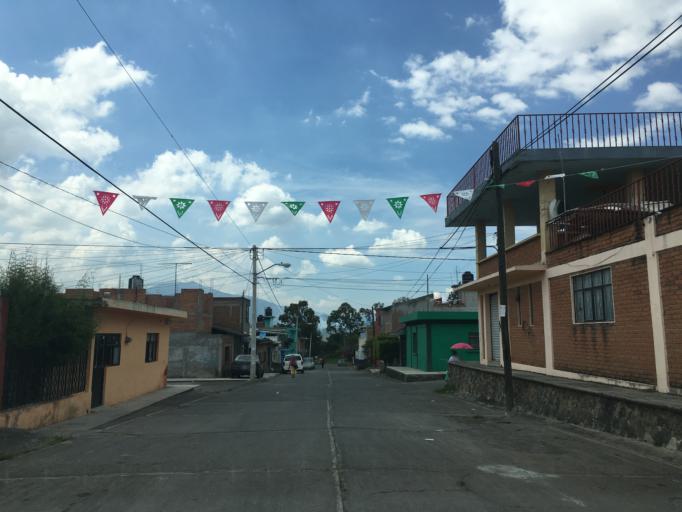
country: MX
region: Michoacan
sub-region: Morelia
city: Morelos
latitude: 19.6492
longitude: -101.2419
